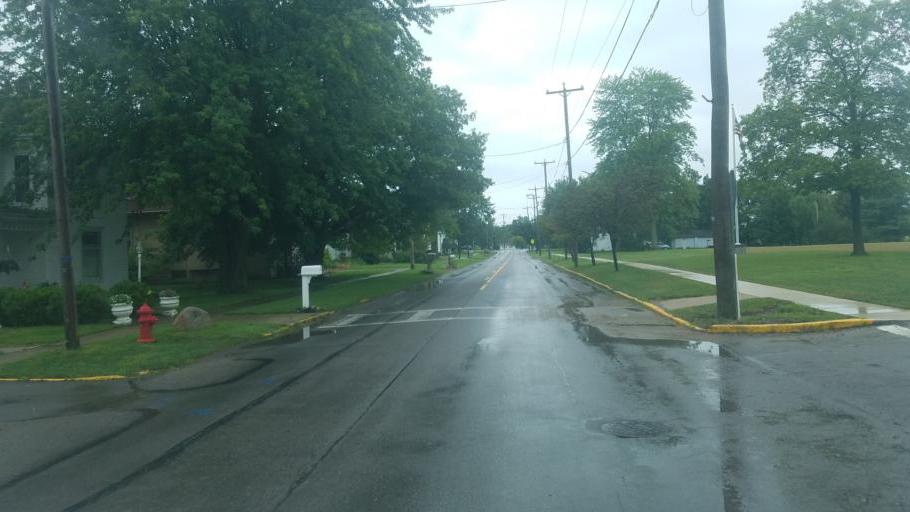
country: US
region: Ohio
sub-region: Hardin County
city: Kenton
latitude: 40.5336
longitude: -83.5232
